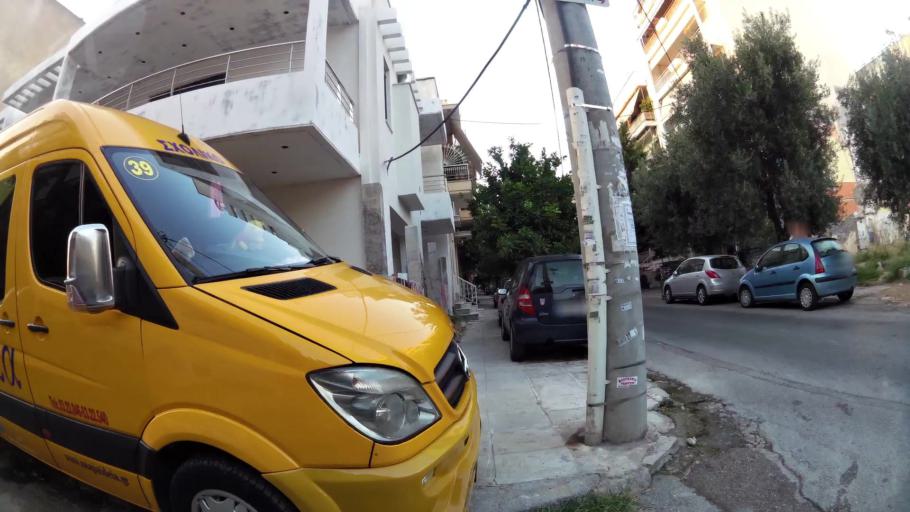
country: GR
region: Attica
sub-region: Nomos Piraios
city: Nikaia
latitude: 37.9709
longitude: 23.6487
